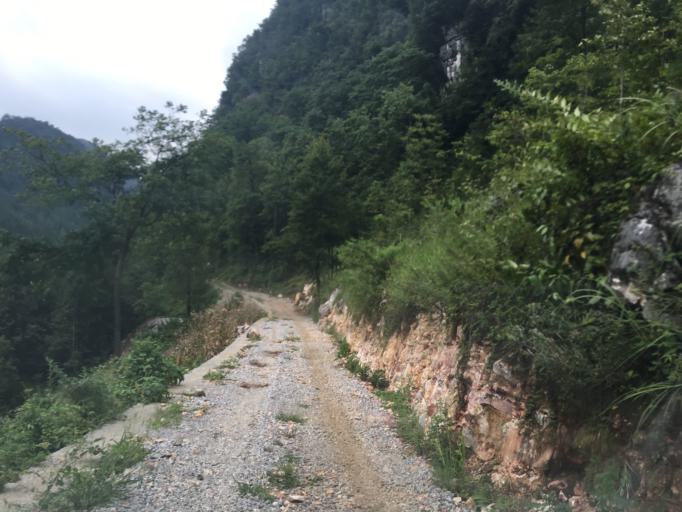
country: CN
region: Guangxi Zhuangzu Zizhiqu
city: Xinzhou
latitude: 25.2204
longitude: 105.6285
